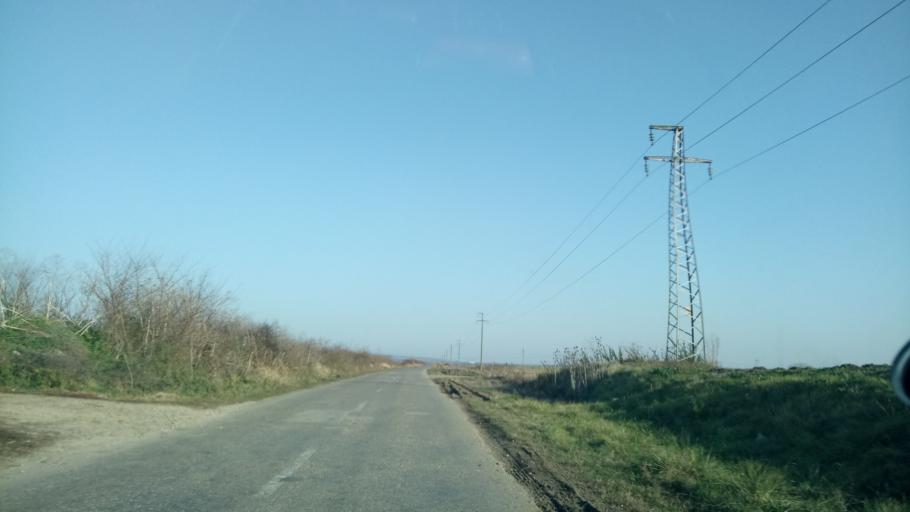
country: RS
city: Krcedin
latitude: 45.1408
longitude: 20.1473
